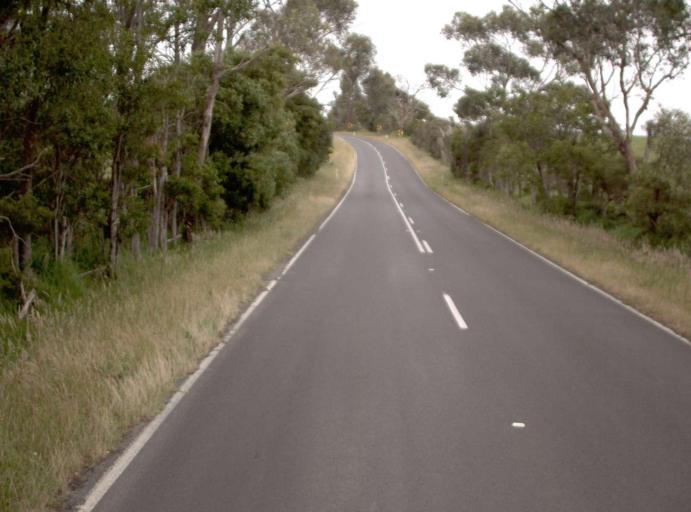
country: AU
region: Victoria
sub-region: Bass Coast
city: North Wonthaggi
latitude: -38.5487
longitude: 145.6602
